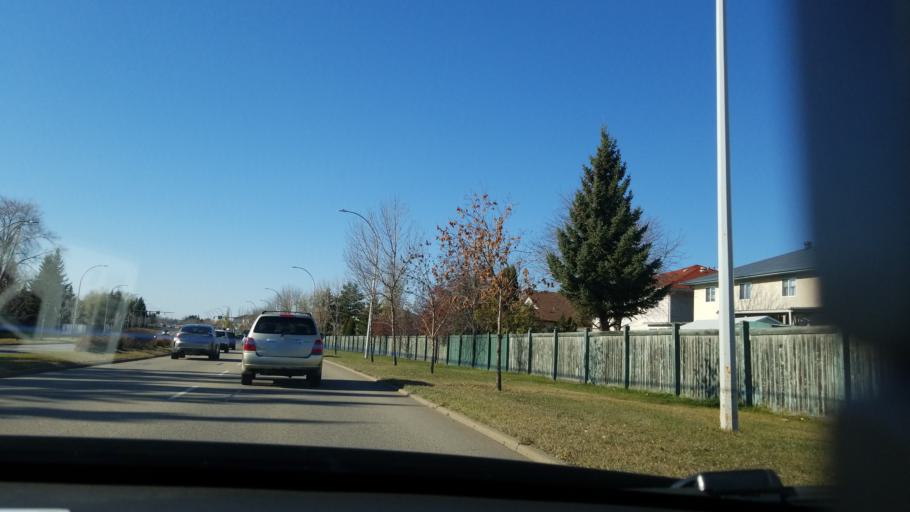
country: CA
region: Alberta
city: Edmonton
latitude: 53.6159
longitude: -113.4731
